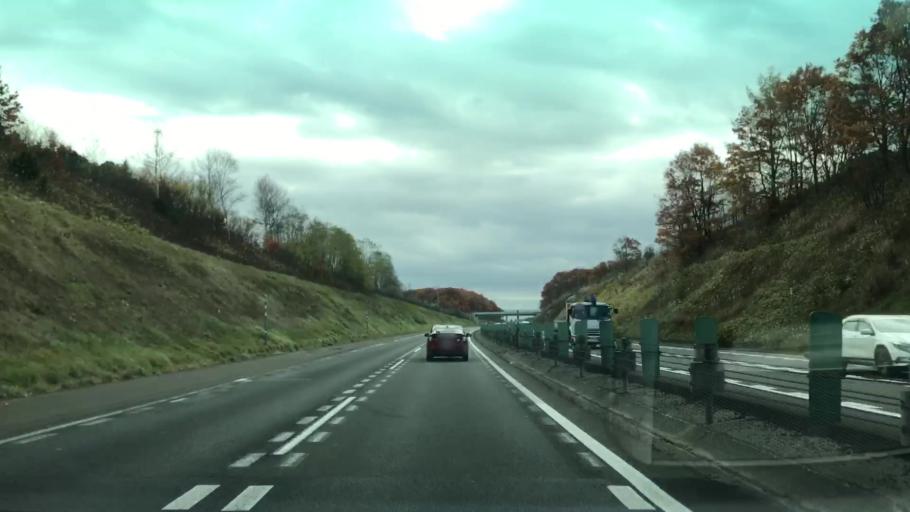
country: JP
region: Hokkaido
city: Kitahiroshima
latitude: 42.9219
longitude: 141.5430
